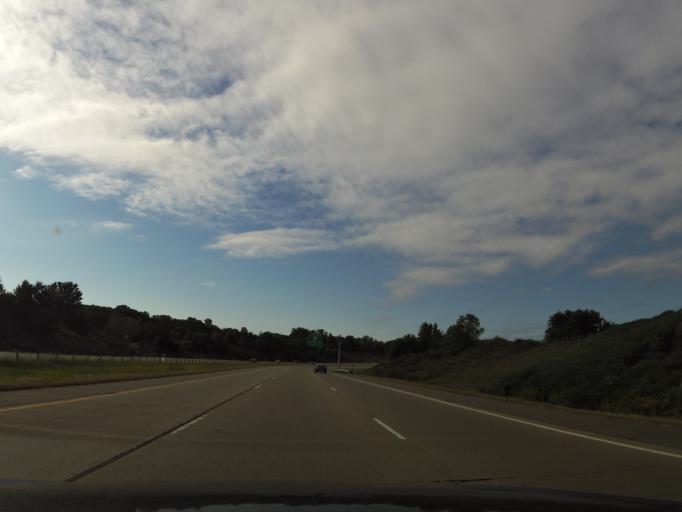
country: US
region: Minnesota
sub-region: Dakota County
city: Eagan
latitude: 44.8206
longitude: -93.1731
